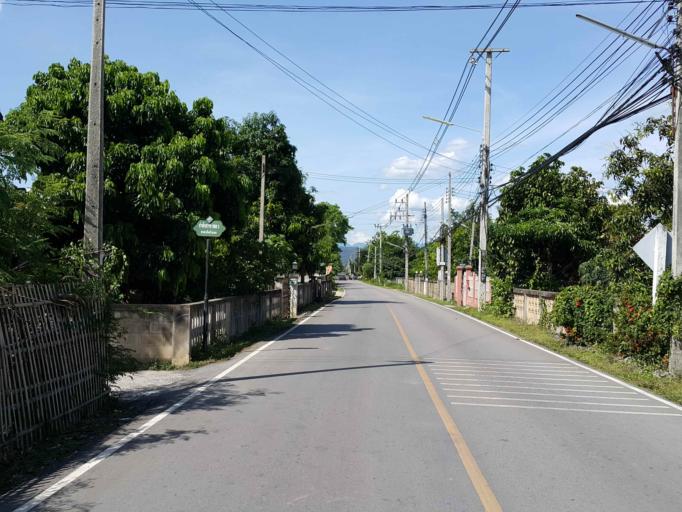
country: TH
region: Chiang Mai
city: San Kamphaeng
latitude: 18.7598
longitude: 99.1396
